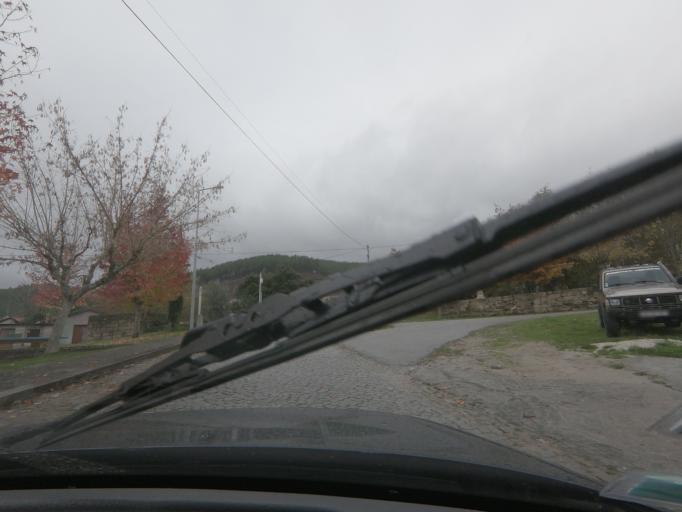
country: PT
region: Vila Real
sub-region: Mondim de Basto
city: Mondim de Basto
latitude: 41.3787
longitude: -7.9515
